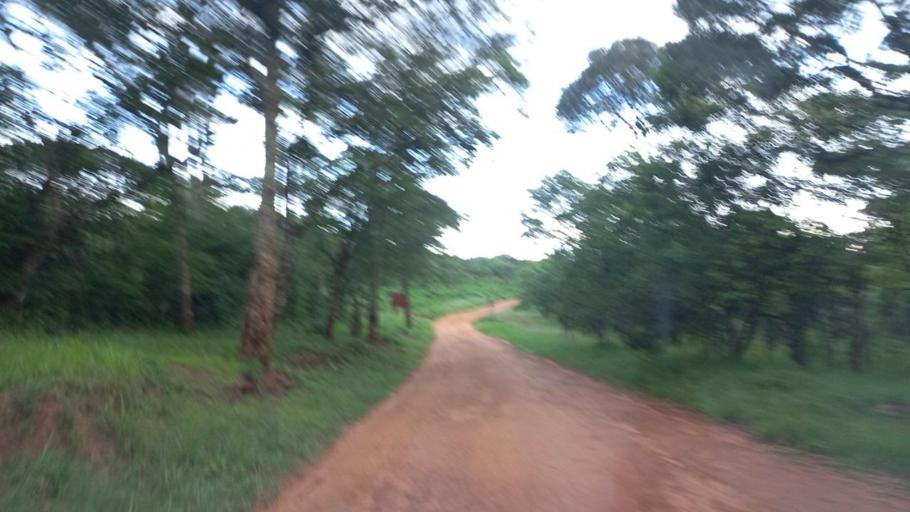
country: ZM
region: North-Western
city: Mwinilunga
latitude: -11.7796
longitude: 24.3760
